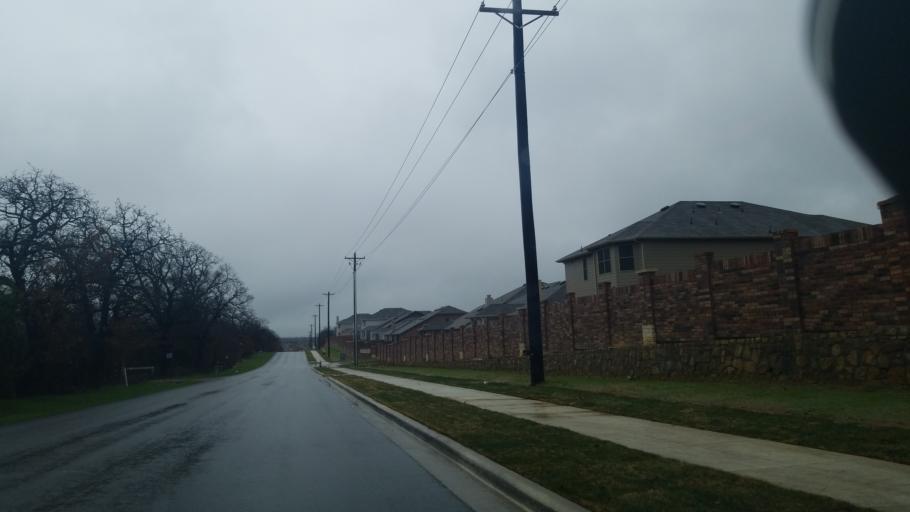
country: US
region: Texas
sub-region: Denton County
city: Corinth
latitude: 33.1781
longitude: -97.0727
